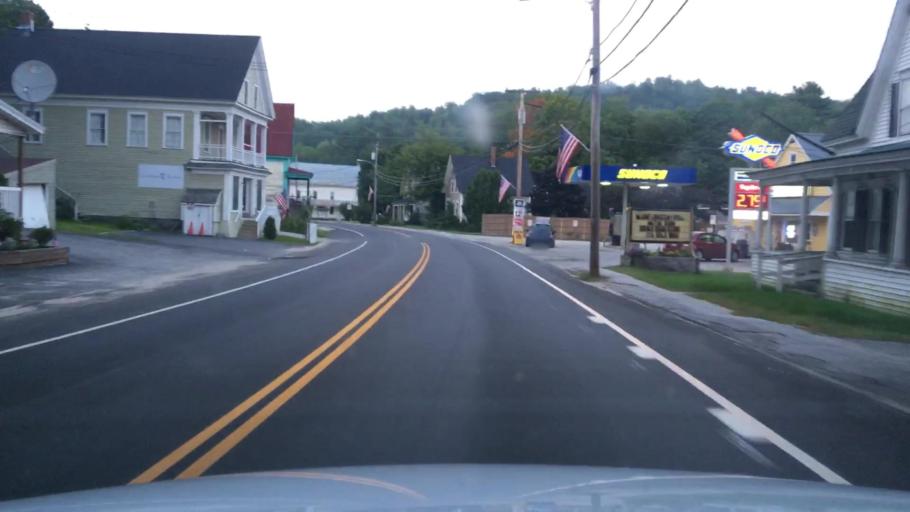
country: US
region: Maine
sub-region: Oxford County
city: West Paris
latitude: 44.3785
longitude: -70.6453
